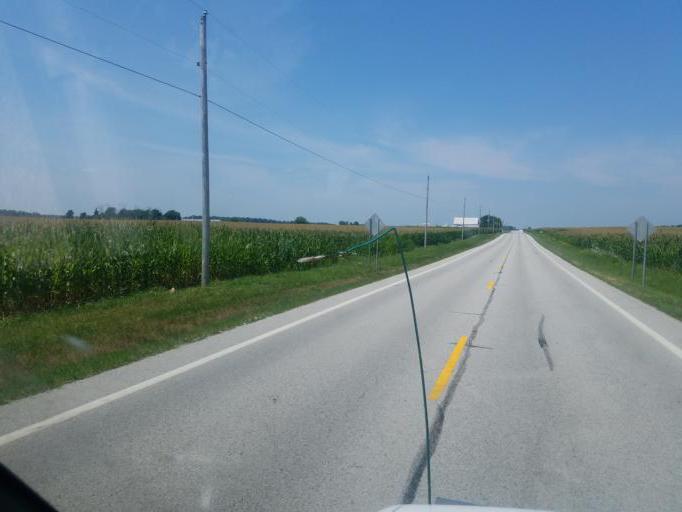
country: US
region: Ohio
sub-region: Auglaize County
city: New Bremen
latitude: 40.4388
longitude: -84.4339
